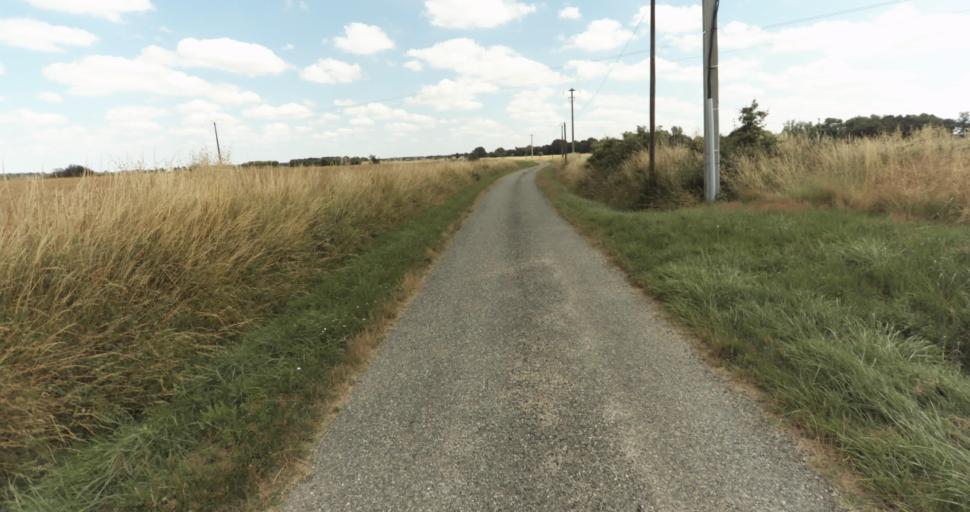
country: FR
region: Midi-Pyrenees
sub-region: Departement de la Haute-Garonne
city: Fontenilles
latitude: 43.5664
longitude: 1.1713
